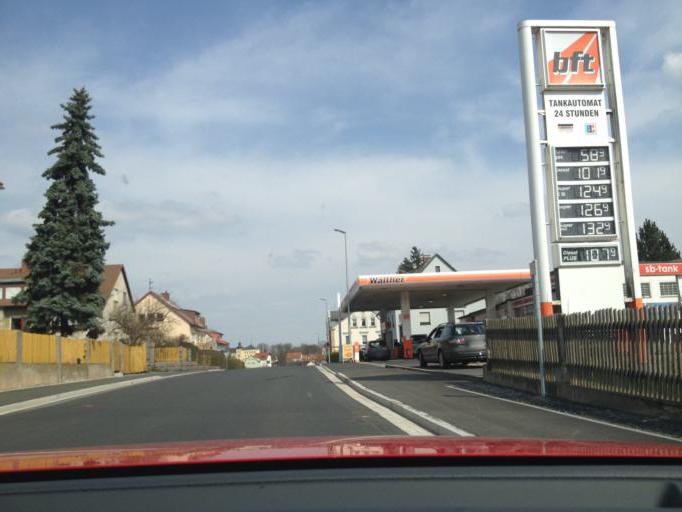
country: DE
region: Bavaria
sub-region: Upper Franconia
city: Arzberg
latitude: 50.0553
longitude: 12.1815
